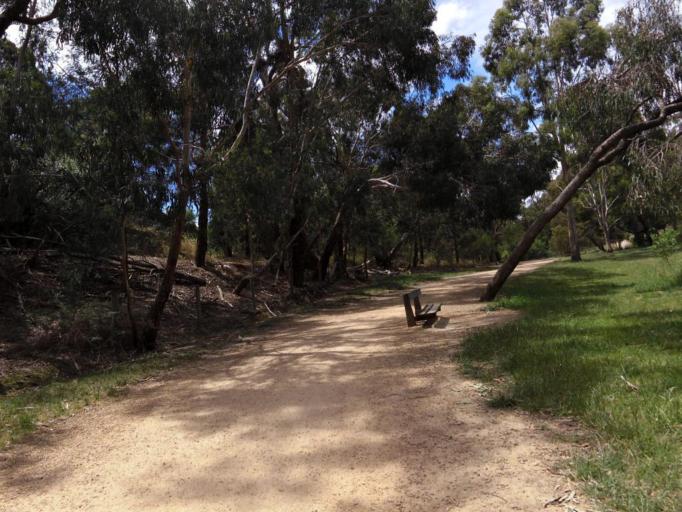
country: AU
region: Victoria
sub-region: Whitehorse
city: Burwood
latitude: -37.8419
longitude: 145.1186
